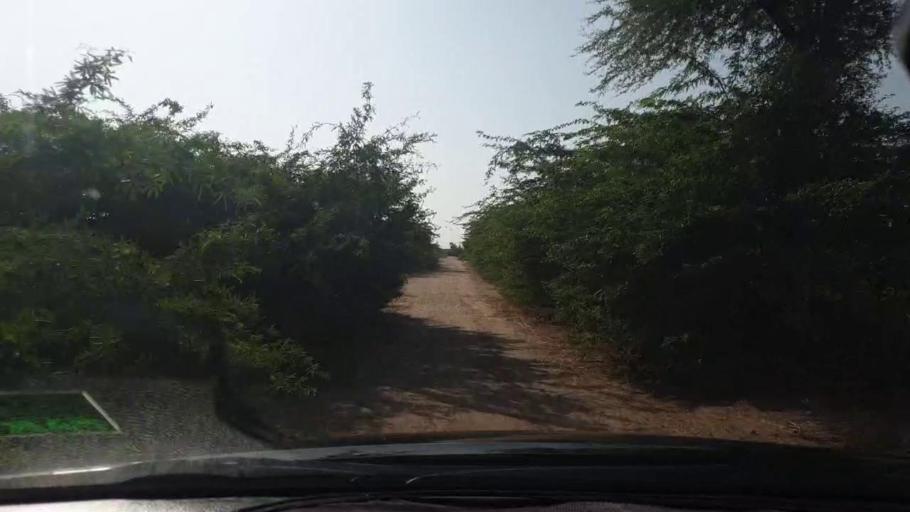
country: PK
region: Sindh
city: Tando Bago
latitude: 24.7211
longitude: 68.9595
